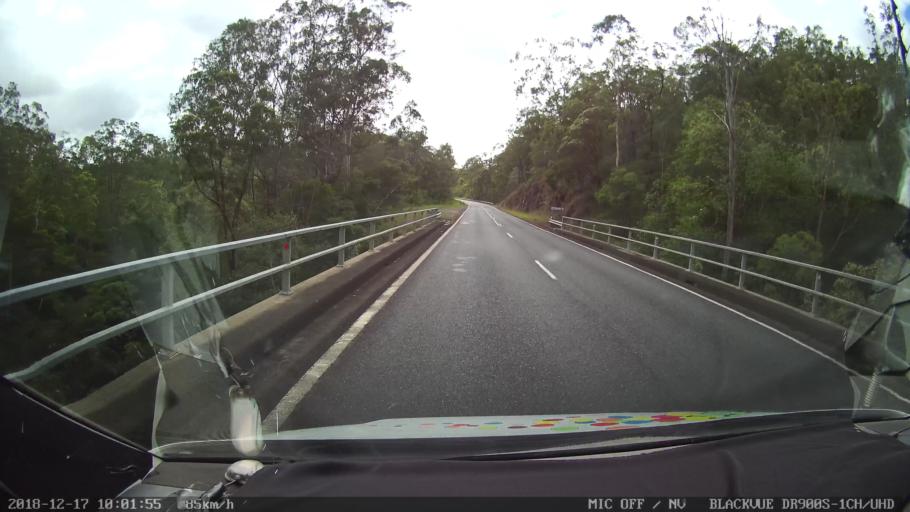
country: AU
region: New South Wales
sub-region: Tenterfield Municipality
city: Carrolls Creek
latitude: -28.9034
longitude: 152.4447
